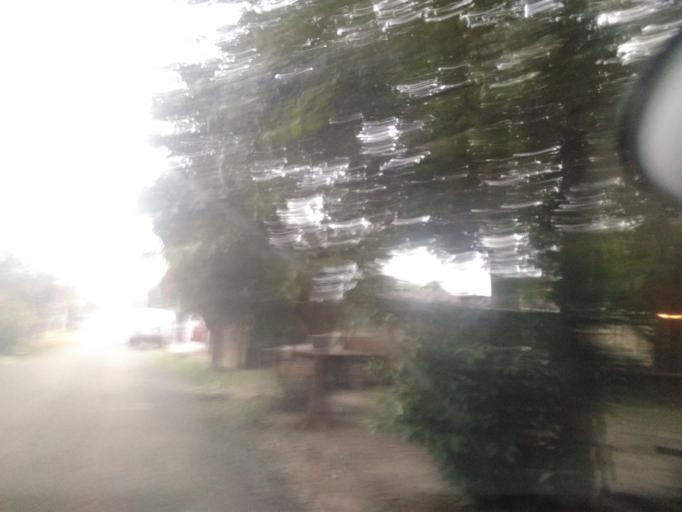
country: AR
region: Chaco
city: Resistencia
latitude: -27.4720
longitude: -58.9880
